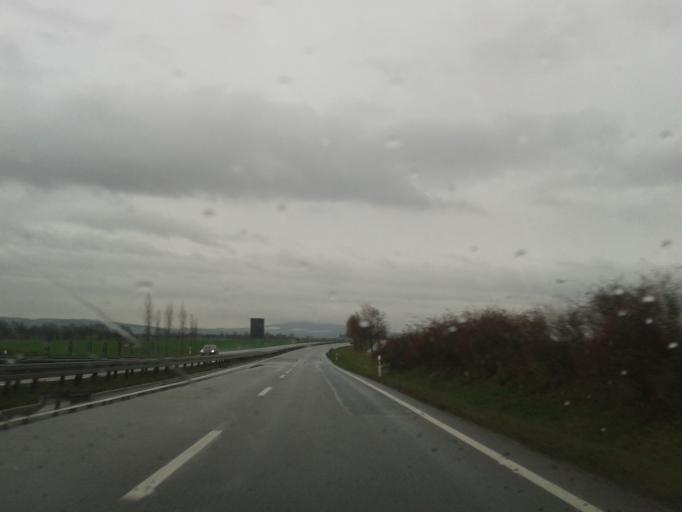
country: DE
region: Saxony
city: Lobau
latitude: 51.1084
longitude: 14.6488
